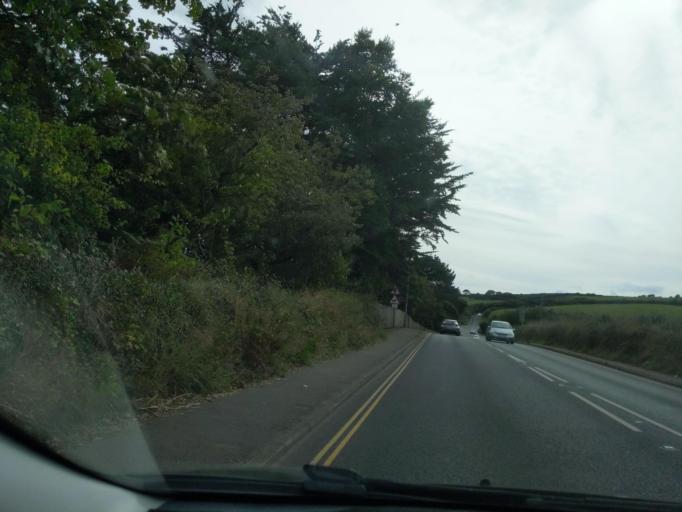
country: GB
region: England
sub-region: Cornwall
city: Mevagissey
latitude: 50.2912
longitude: -4.7861
